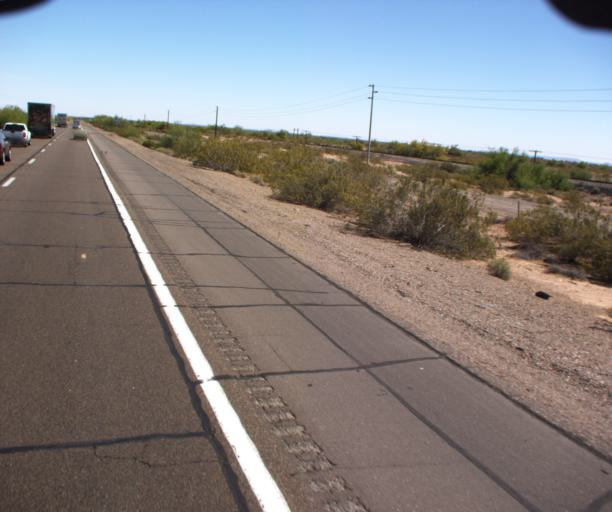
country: US
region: Arizona
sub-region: Yuma County
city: Wellton
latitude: 32.8253
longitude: -113.4351
